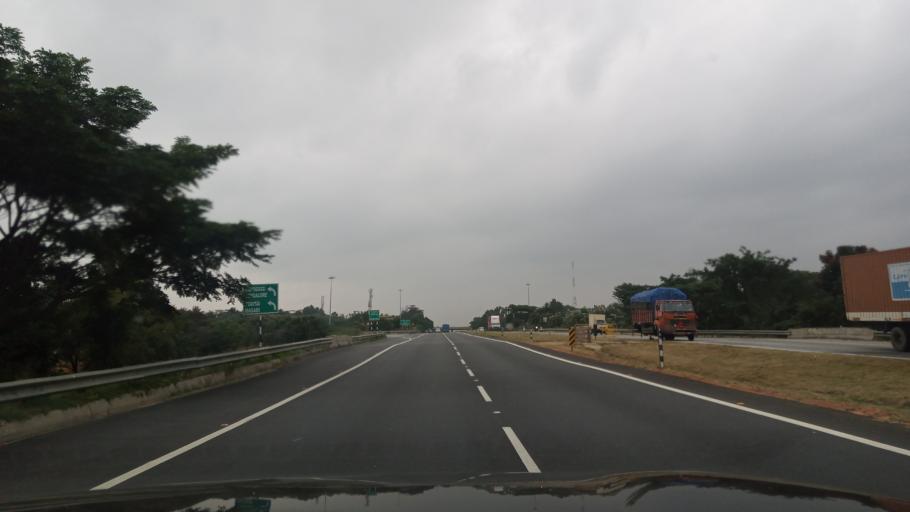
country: IN
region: Karnataka
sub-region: Bangalore Urban
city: Bangalore
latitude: 12.9940
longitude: 77.4733
